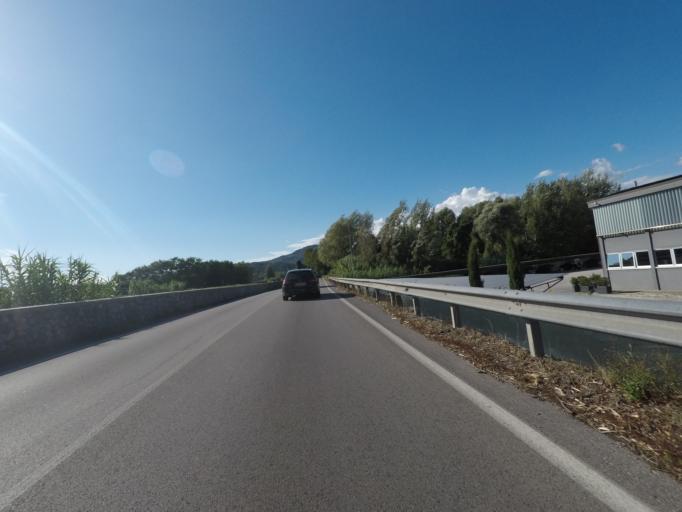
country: IT
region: Tuscany
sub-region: Provincia di Lucca
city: Lucca
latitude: 43.8710
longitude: 10.4995
